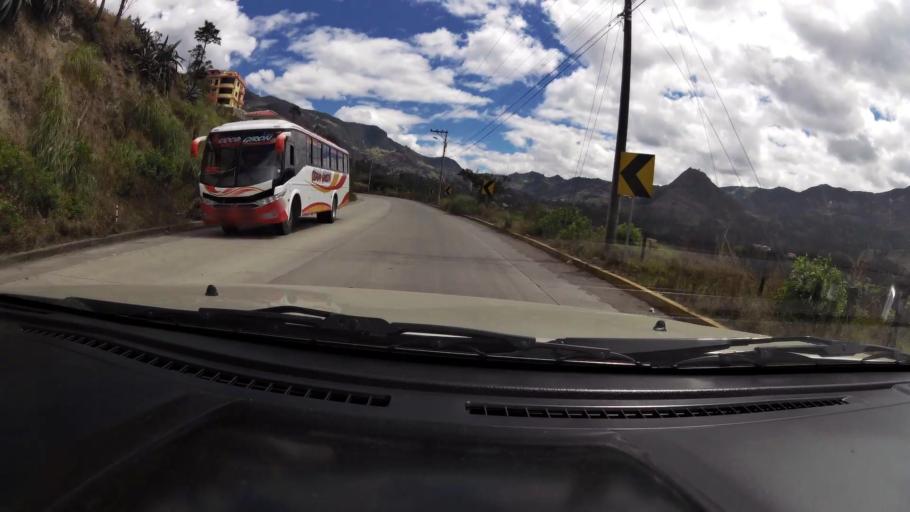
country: EC
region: Azuay
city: Cuenca
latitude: -3.1538
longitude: -79.1464
